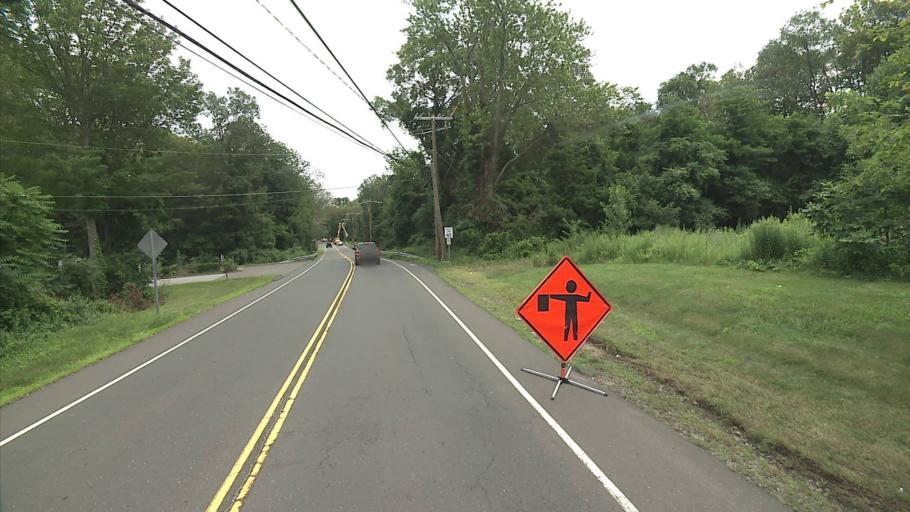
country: US
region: Connecticut
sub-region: New Haven County
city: Madison
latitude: 41.3577
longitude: -72.5638
